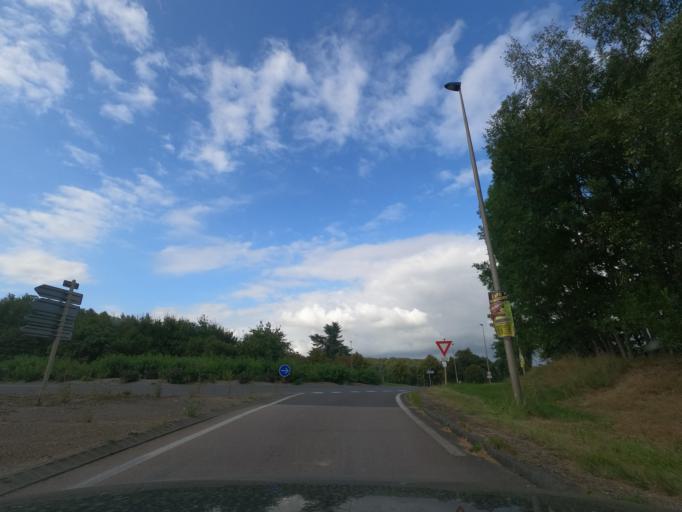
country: FR
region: Haute-Normandie
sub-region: Departement de l'Eure
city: Bernay
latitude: 49.0822
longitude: 0.5740
